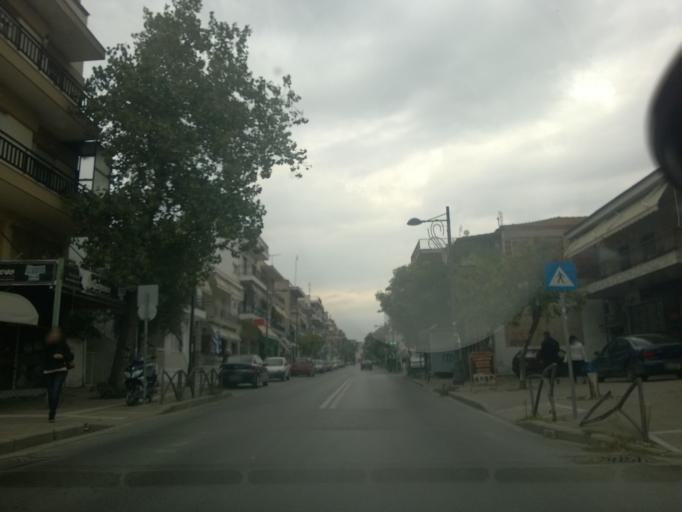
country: GR
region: Central Macedonia
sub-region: Nomos Thessalonikis
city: Stavroupoli
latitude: 40.6694
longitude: 22.9331
